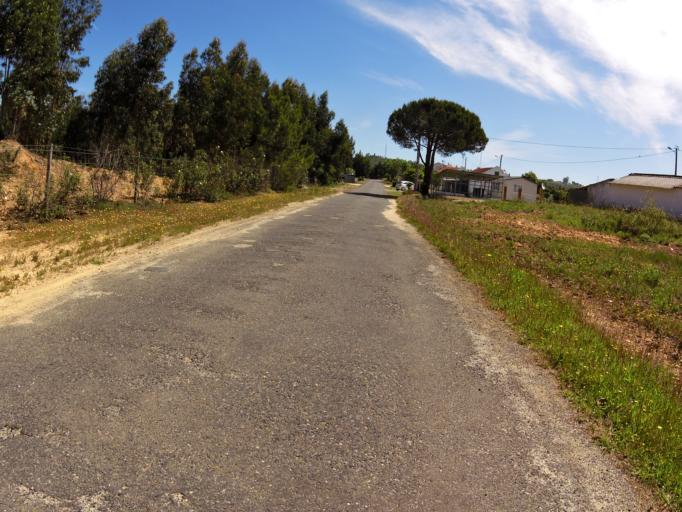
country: PT
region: Setubal
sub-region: Santiago do Cacem
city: Santiago do Cacem
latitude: 37.9446
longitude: -8.7307
